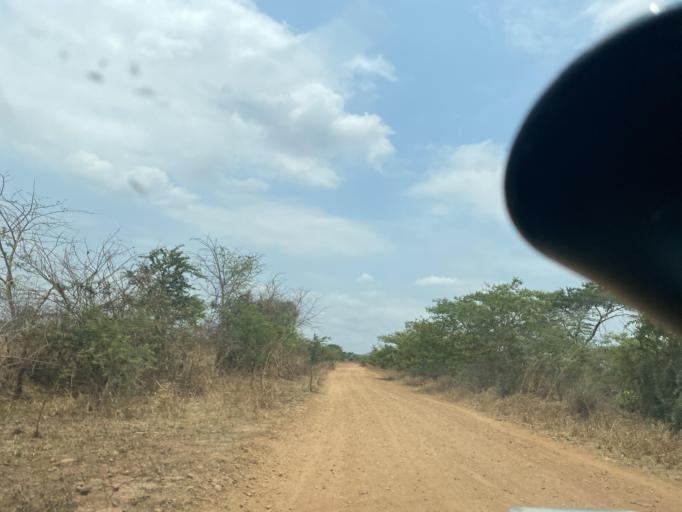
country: ZM
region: Lusaka
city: Chongwe
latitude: -15.5260
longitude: 28.8237
